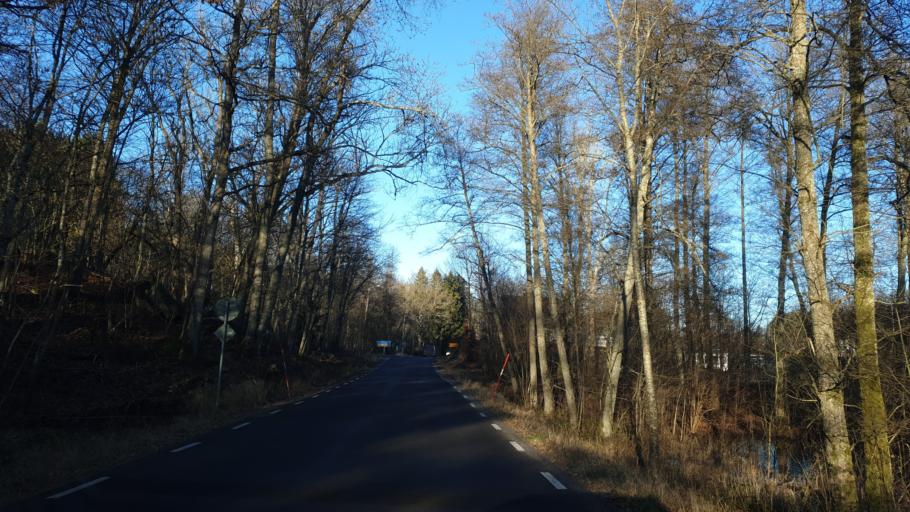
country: SE
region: Blekinge
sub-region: Karlskrona Kommun
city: Nattraby
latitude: 56.2552
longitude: 15.5128
